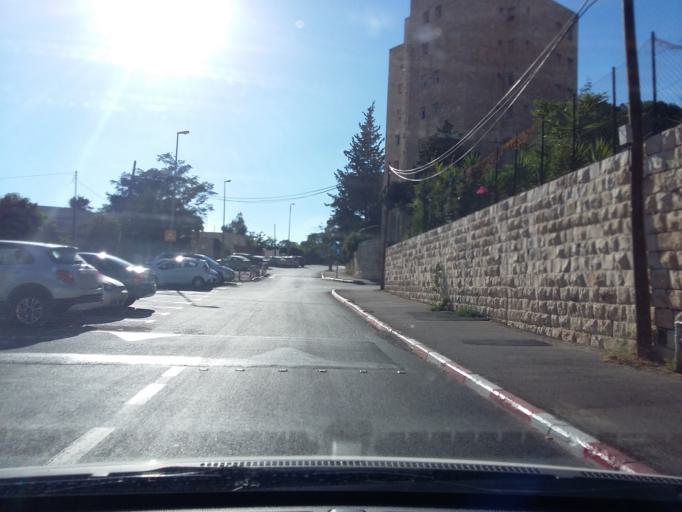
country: PS
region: West Bank
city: East Jerusalem
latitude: 31.8009
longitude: 35.2363
